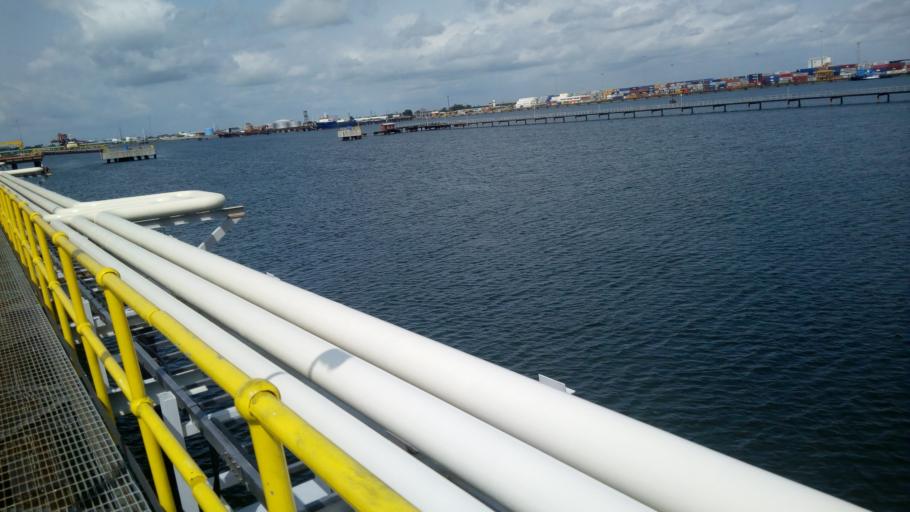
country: LR
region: Montserrado
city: Monrovia
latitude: 6.3409
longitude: -10.8033
